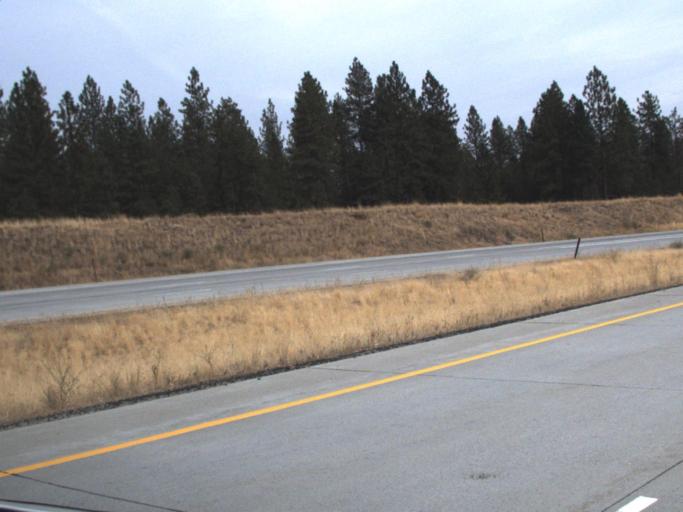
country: US
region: Washington
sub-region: Spokane County
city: Mead
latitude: 47.7779
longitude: -117.3778
